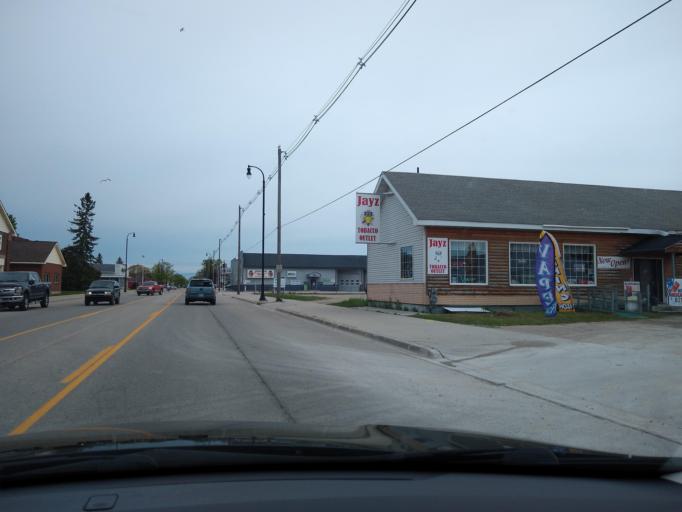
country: US
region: Michigan
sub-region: Delta County
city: Escanaba
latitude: 45.7503
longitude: -87.0718
